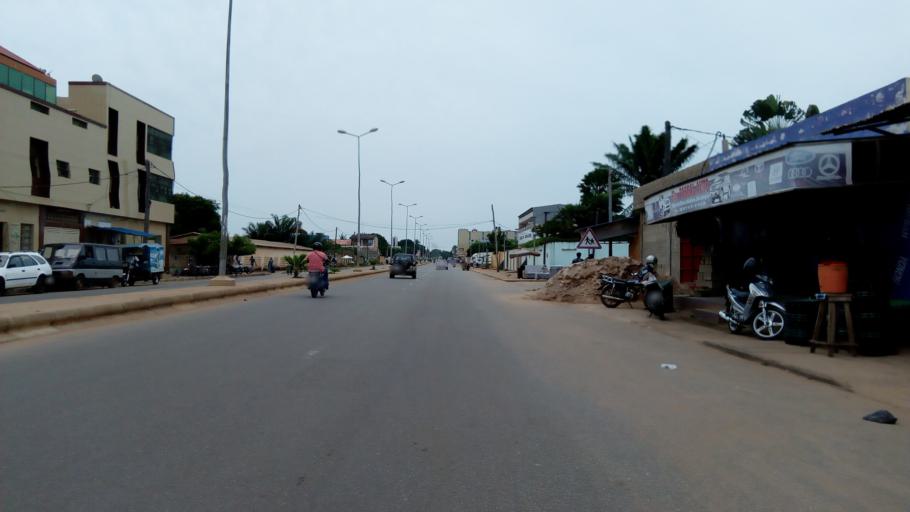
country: TG
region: Maritime
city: Lome
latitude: 6.1614
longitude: 1.2329
